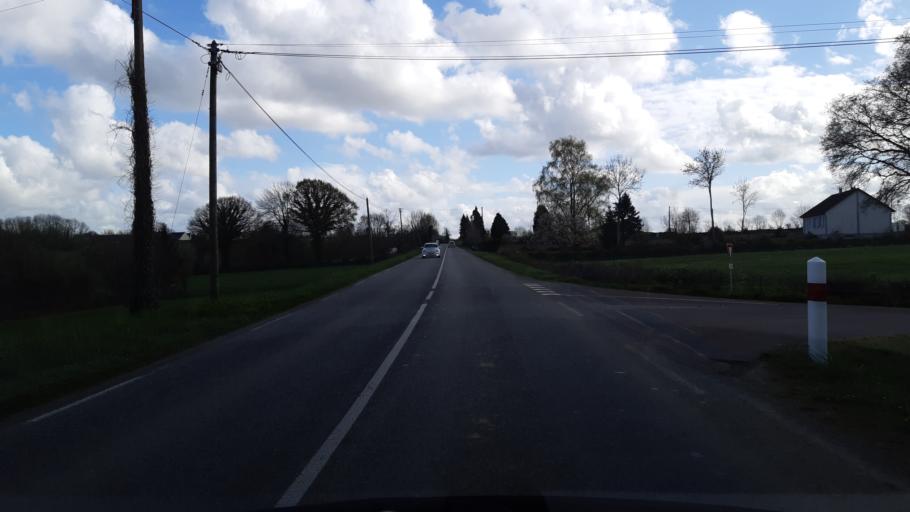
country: FR
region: Lower Normandy
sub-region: Departement de la Manche
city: Agneaux
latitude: 49.0585
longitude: -1.1333
